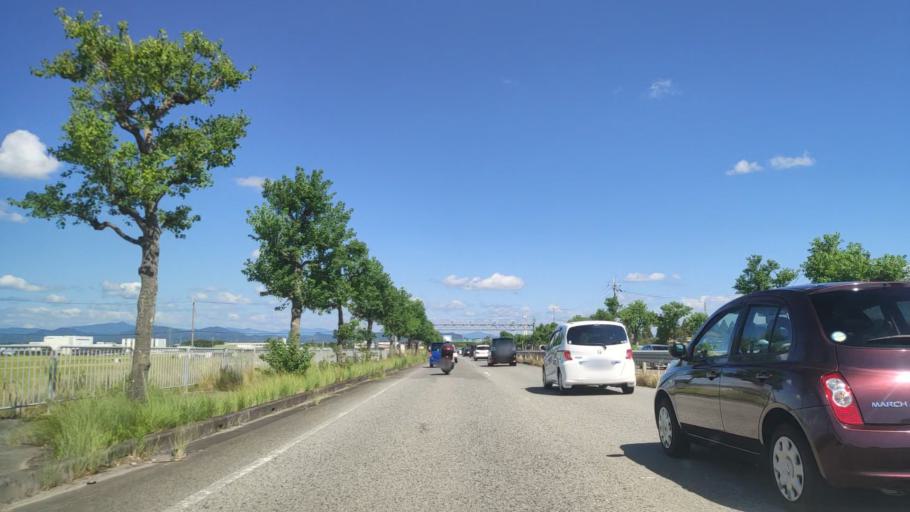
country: JP
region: Hyogo
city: Ono
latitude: 34.8650
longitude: 134.9522
